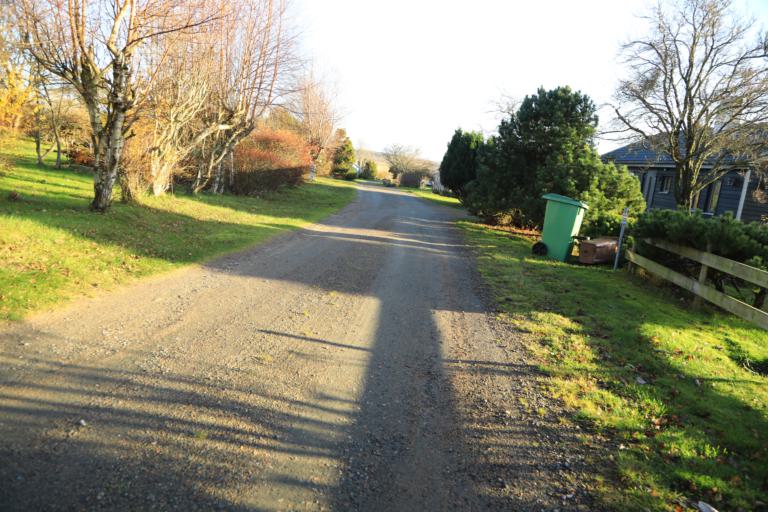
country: SE
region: Halland
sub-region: Varbergs Kommun
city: Varberg
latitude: 57.1683
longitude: 12.2184
